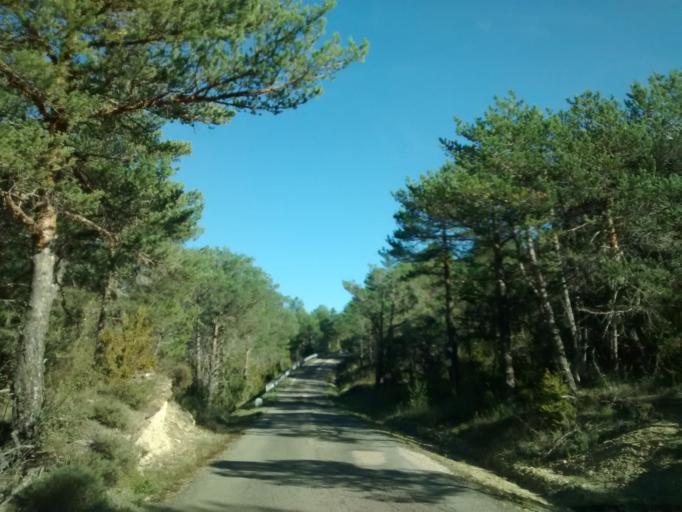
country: ES
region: Aragon
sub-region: Provincia de Huesca
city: Santa Cruz de la Seros
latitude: 42.4320
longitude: -0.6279
